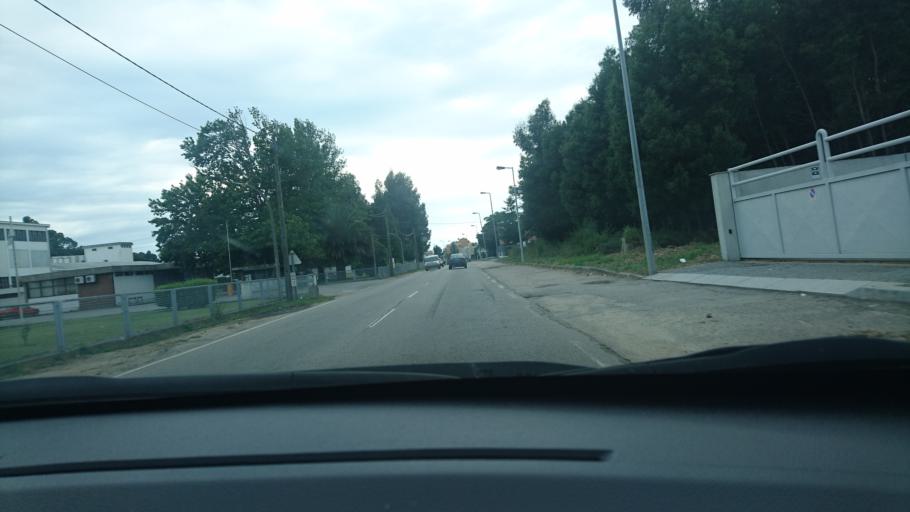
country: PT
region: Aveiro
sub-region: Santa Maria da Feira
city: Rio Meao
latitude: 40.9598
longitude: -8.5950
